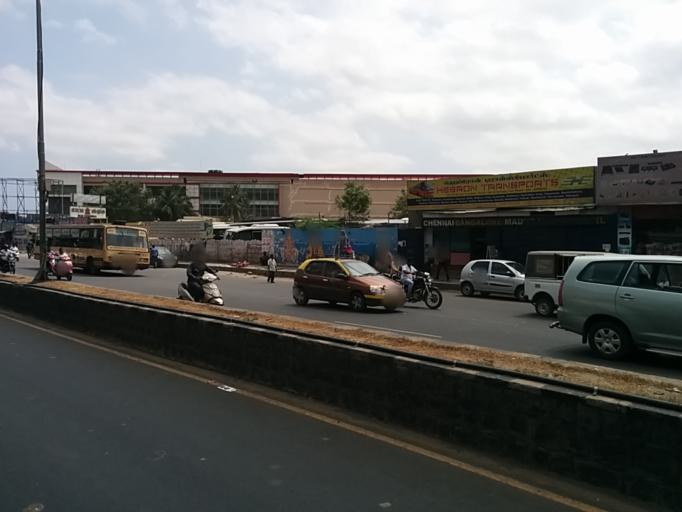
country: IN
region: Tamil Nadu
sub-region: Chennai
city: Chetput
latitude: 13.0720
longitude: 80.2025
